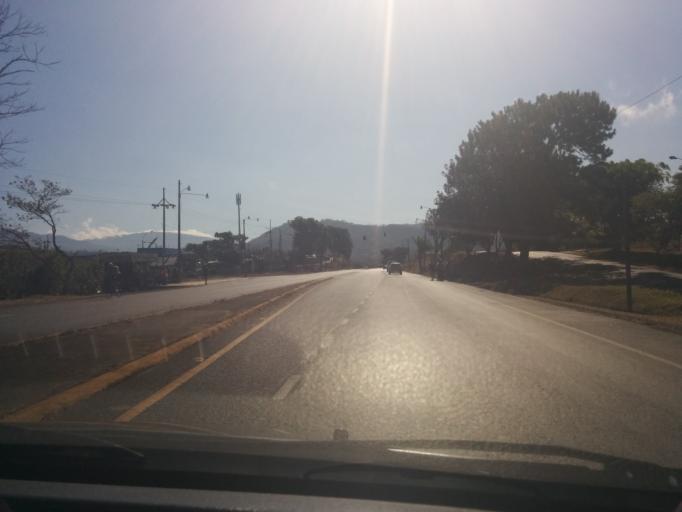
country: CR
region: Alajuela
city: San Ramon
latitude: 10.0764
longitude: -84.4714
